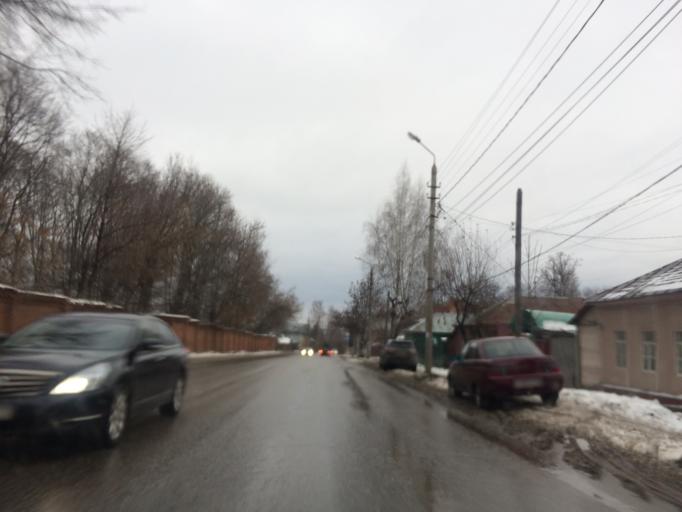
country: RU
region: Tula
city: Tula
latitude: 54.1790
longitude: 37.6157
